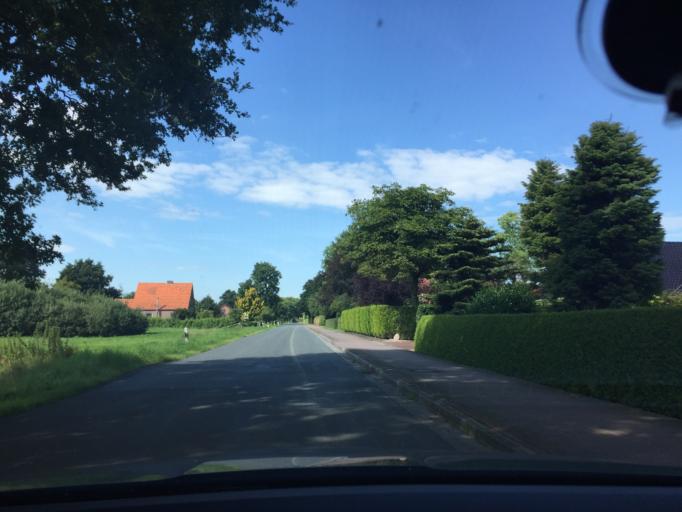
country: DE
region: Lower Saxony
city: Rechtsupweg
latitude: 53.5016
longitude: 7.3489
